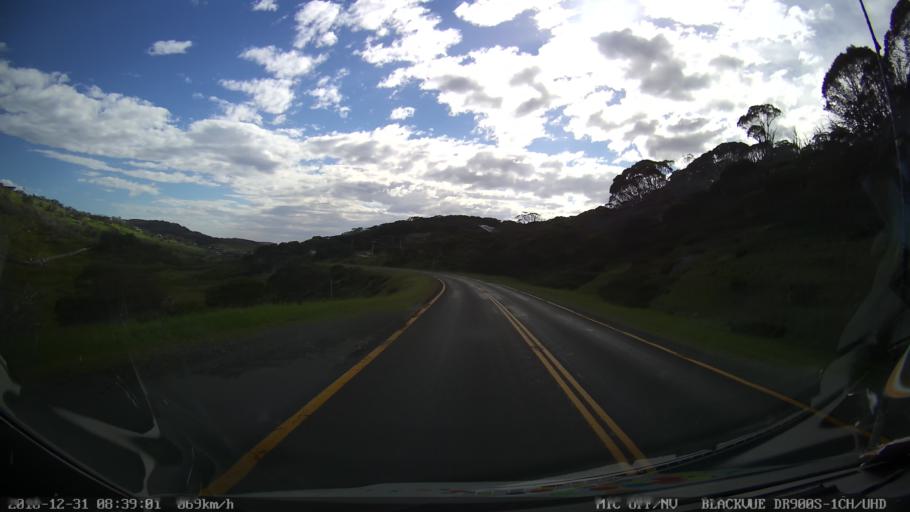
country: AU
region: New South Wales
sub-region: Snowy River
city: Jindabyne
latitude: -36.4114
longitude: 148.4018
